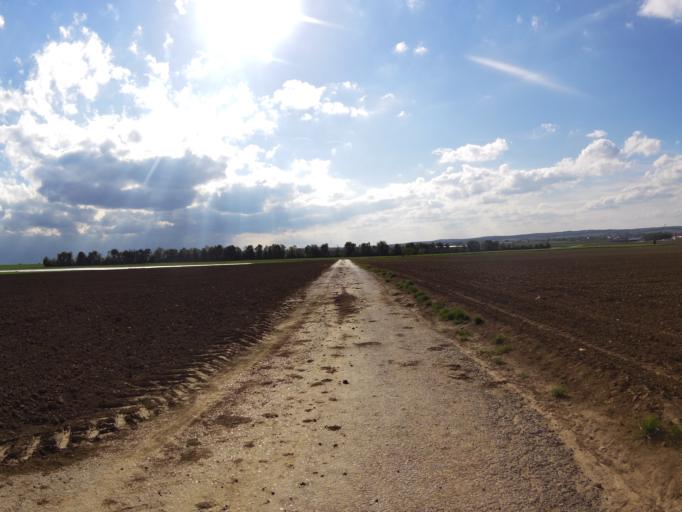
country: DE
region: Bavaria
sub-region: Regierungsbezirk Unterfranken
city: Oberpleichfeld
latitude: 49.8565
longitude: 10.0734
